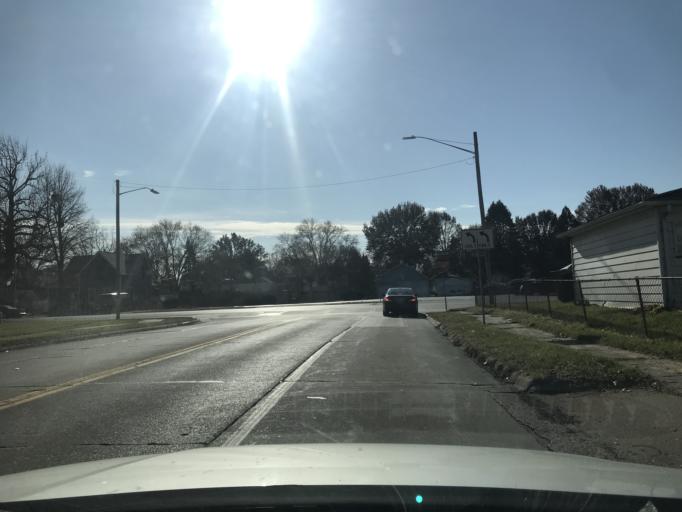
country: US
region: Iowa
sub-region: Scott County
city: Davenport
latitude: 41.5227
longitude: -90.6145
